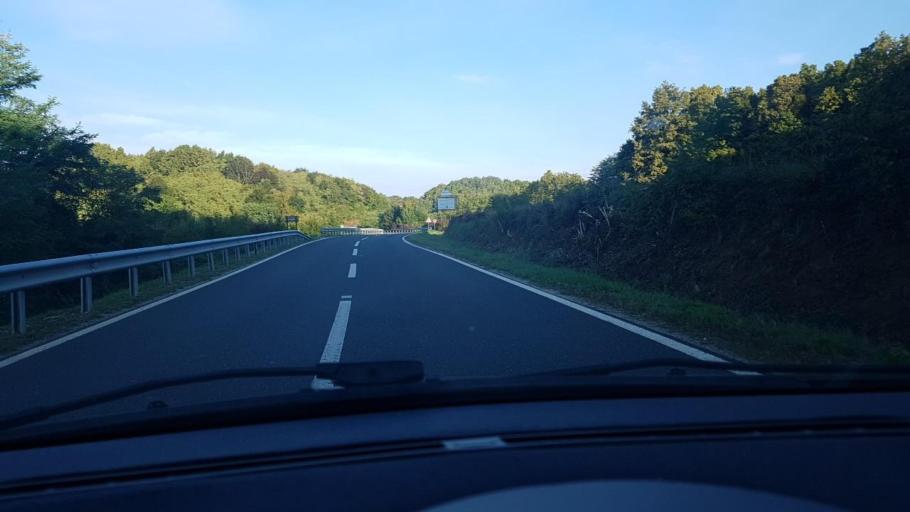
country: HR
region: Krapinsko-Zagorska
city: Marija Bistrica
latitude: 45.9546
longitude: 16.0957
